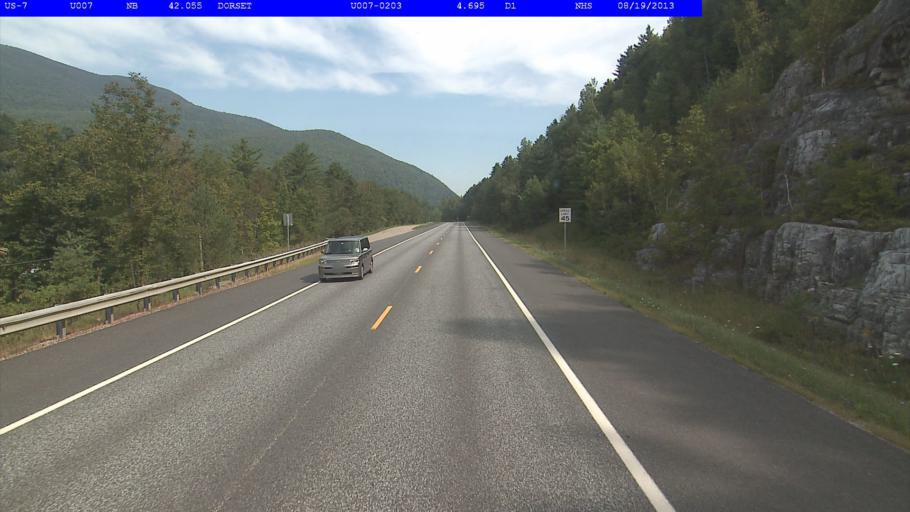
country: US
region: Vermont
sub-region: Bennington County
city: Manchester Center
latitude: 43.2764
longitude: -73.0036
